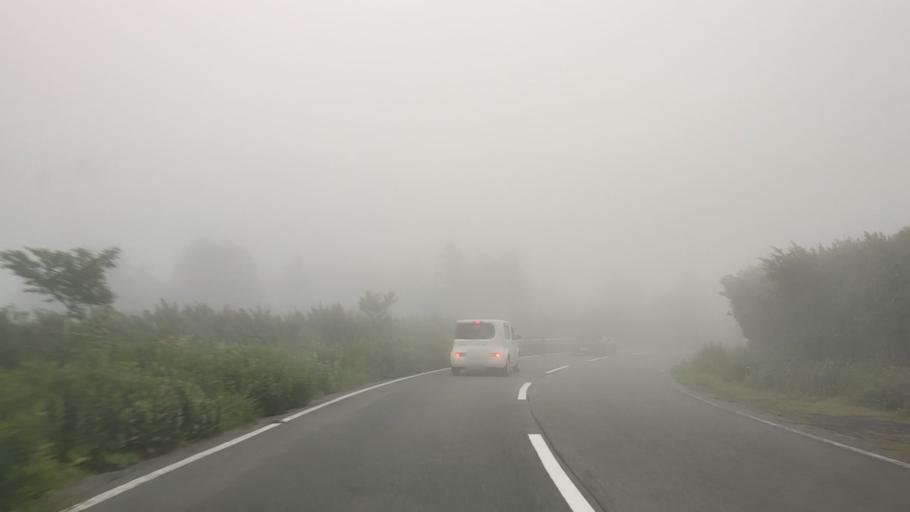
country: JP
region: Kanagawa
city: Hakone
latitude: 35.1936
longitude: 138.9987
